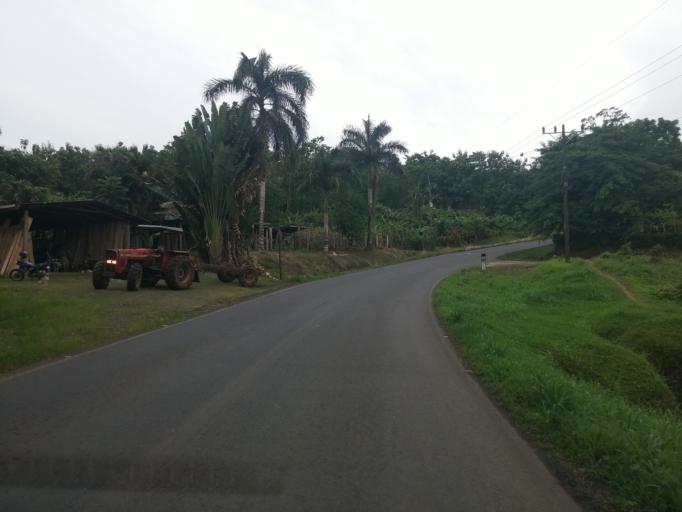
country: CR
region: Alajuela
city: Upala
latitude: 10.8135
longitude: -85.0222
